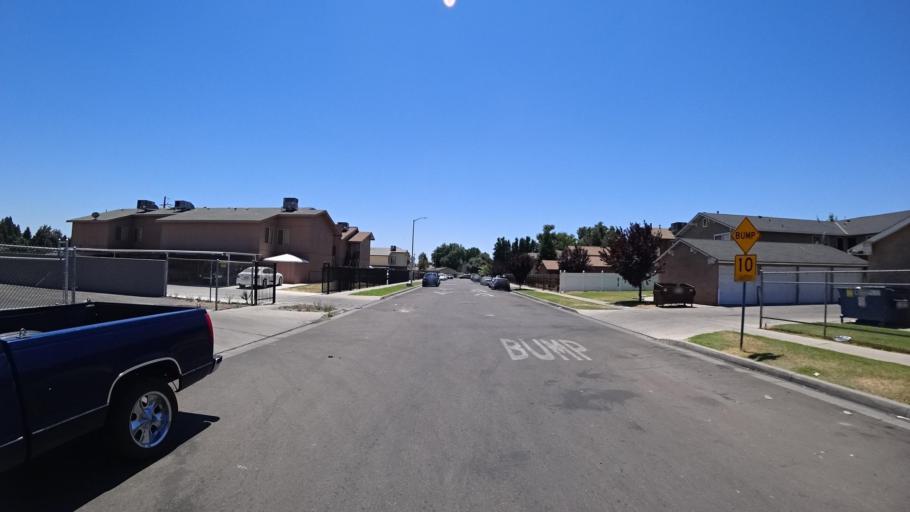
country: US
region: California
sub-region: Fresno County
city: Sunnyside
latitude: 36.7351
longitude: -119.7256
